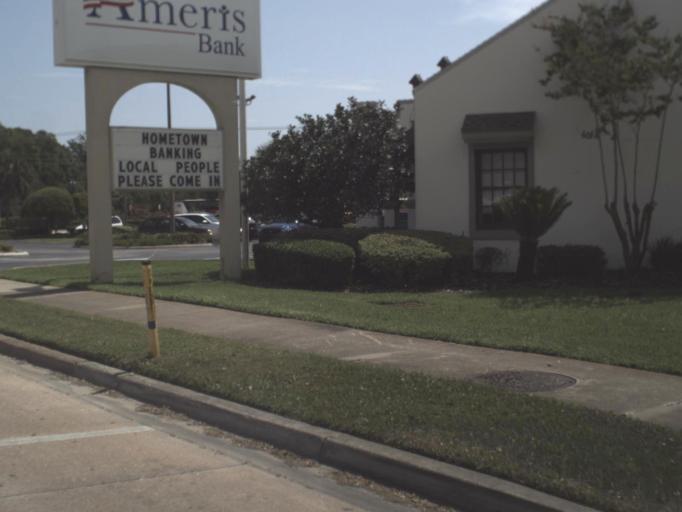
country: US
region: Florida
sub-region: Saint Johns County
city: Saint Augustine
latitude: 29.8981
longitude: -81.3201
